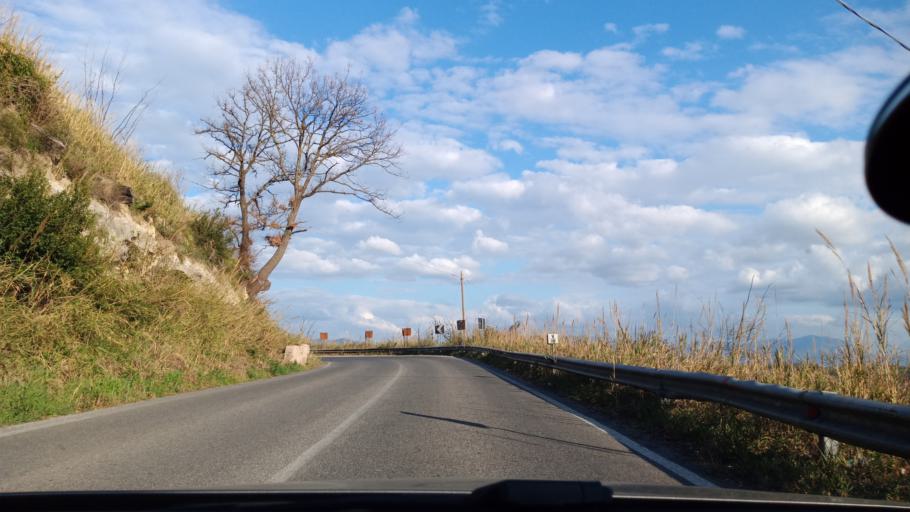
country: IT
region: Latium
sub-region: Citta metropolitana di Roma Capitale
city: Nazzano
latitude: 42.2065
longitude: 12.6046
